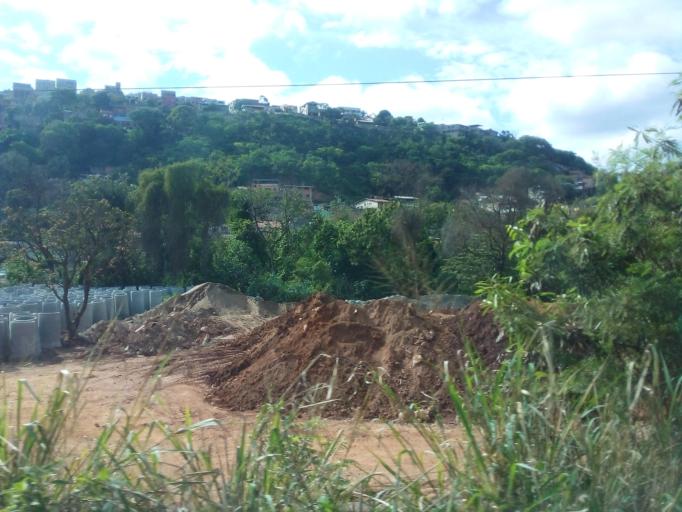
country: BR
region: Minas Gerais
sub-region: Belo Horizonte
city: Belo Horizonte
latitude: -19.8831
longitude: -43.8603
